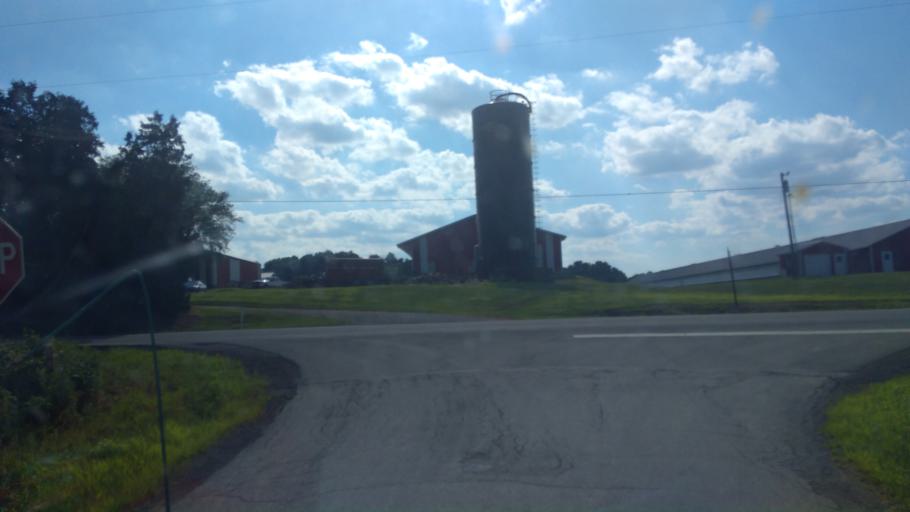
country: US
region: Ohio
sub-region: Wayne County
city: Dalton
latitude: 40.7535
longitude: -81.6909
